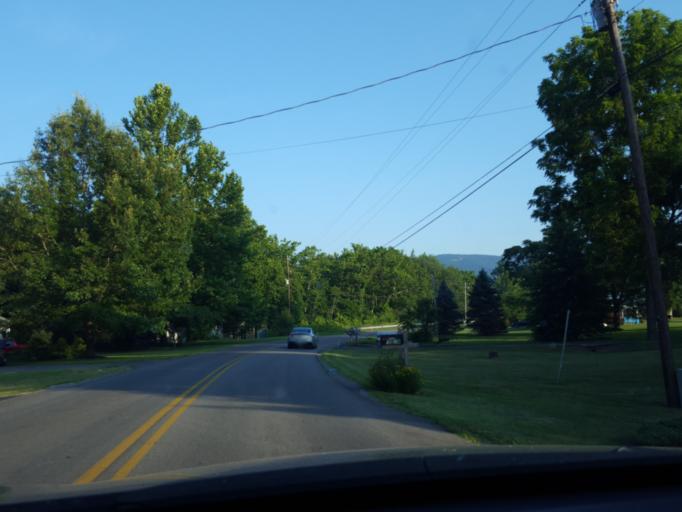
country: US
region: Virginia
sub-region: Augusta County
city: Lyndhurst
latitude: 37.9841
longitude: -78.9545
